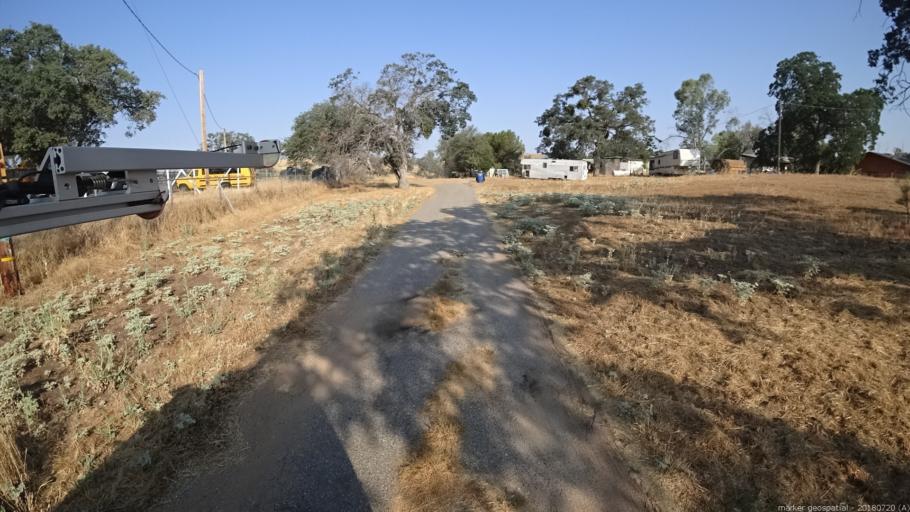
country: US
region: California
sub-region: Madera County
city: Yosemite Lakes
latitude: 37.2124
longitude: -119.9092
